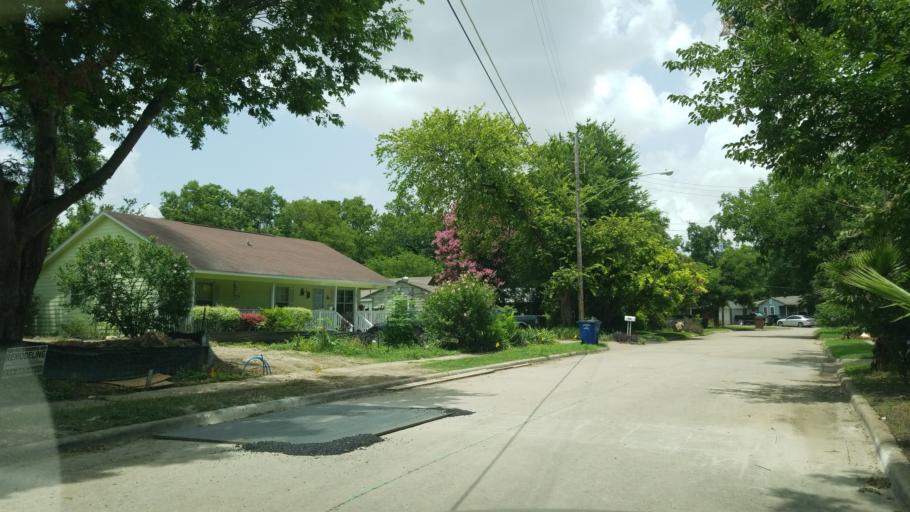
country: US
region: Texas
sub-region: Dallas County
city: Cockrell Hill
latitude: 32.7889
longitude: -96.8946
